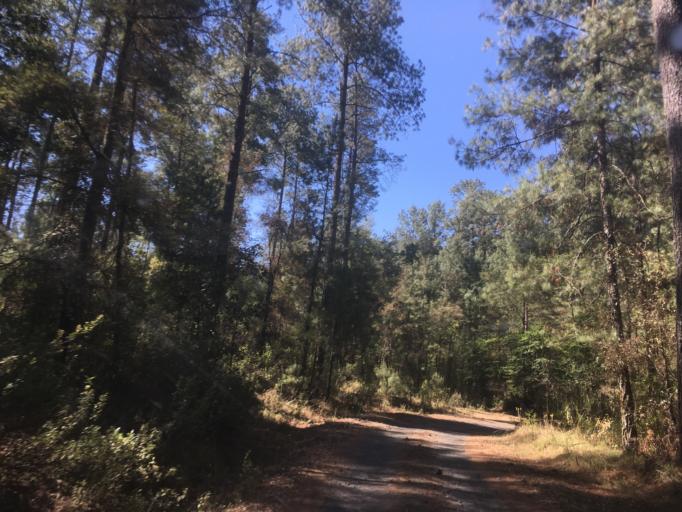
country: MX
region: Michoacan
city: Angahuan
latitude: 19.4900
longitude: -102.2016
